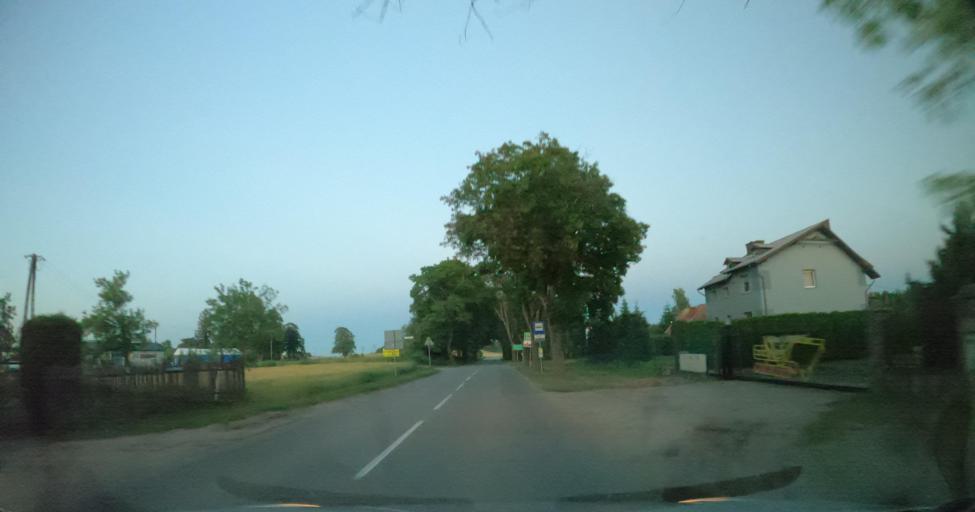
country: PL
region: Pomeranian Voivodeship
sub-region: Powiat wejherowski
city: Szemud
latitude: 54.4712
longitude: 18.2770
